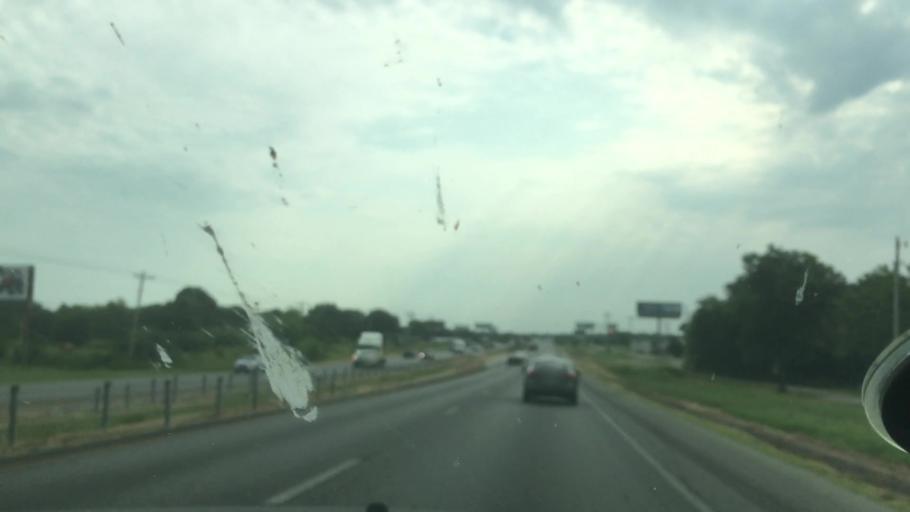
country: US
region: Oklahoma
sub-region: Bryan County
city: Calera
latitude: 33.9142
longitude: -96.4546
